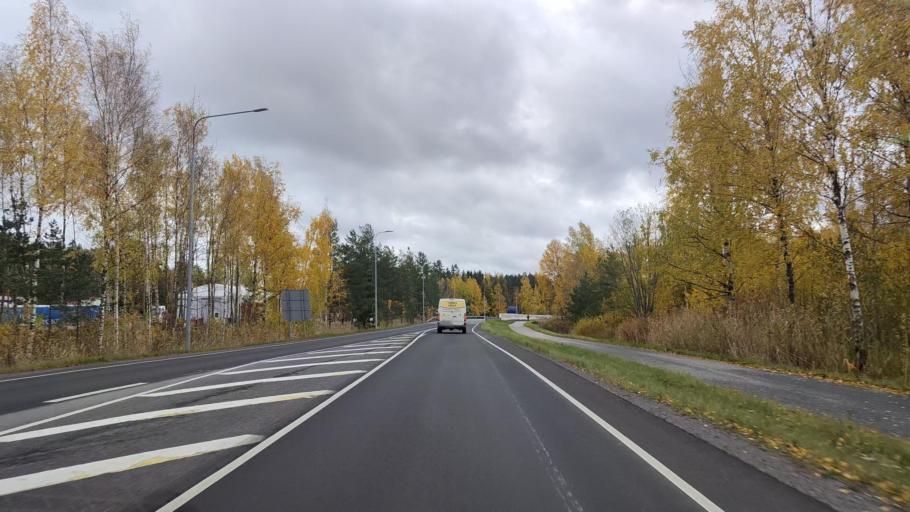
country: FI
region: Varsinais-Suomi
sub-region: Turku
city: Kaarina
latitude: 60.4323
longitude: 22.3845
